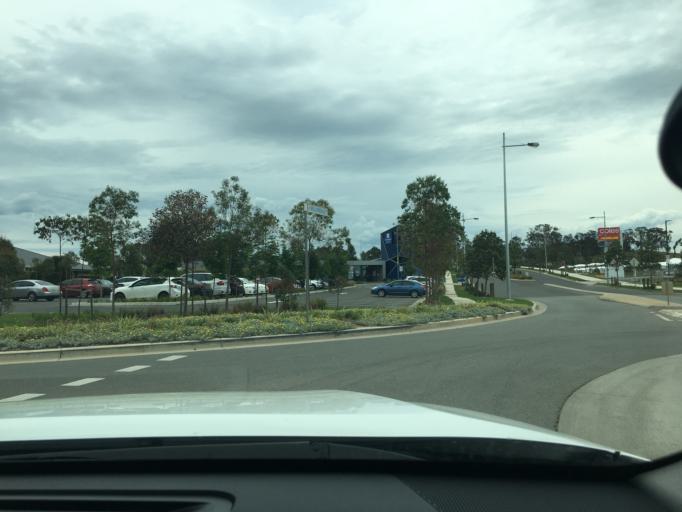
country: AU
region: New South Wales
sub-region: Campbelltown Municipality
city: Denham Court
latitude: -33.9780
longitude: 150.8123
